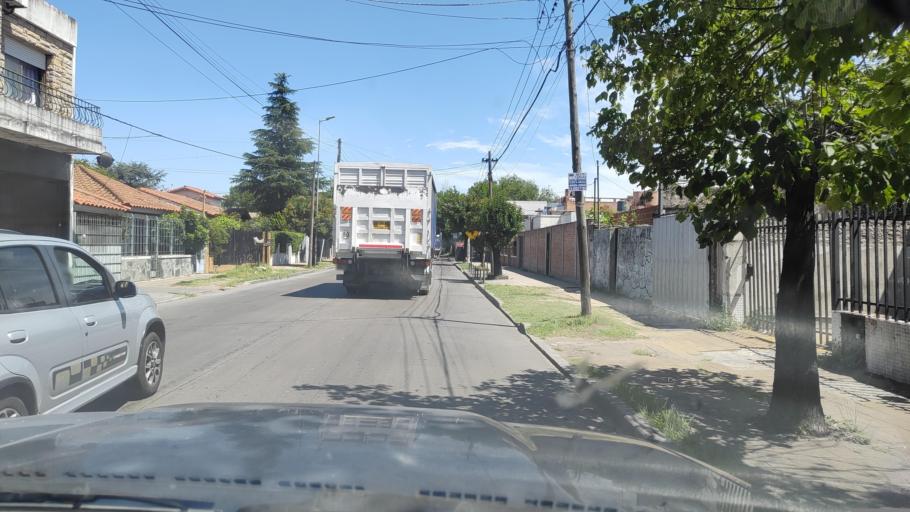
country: AR
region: Buenos Aires
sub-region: Partido de Moron
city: Moron
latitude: -34.6649
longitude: -58.6004
